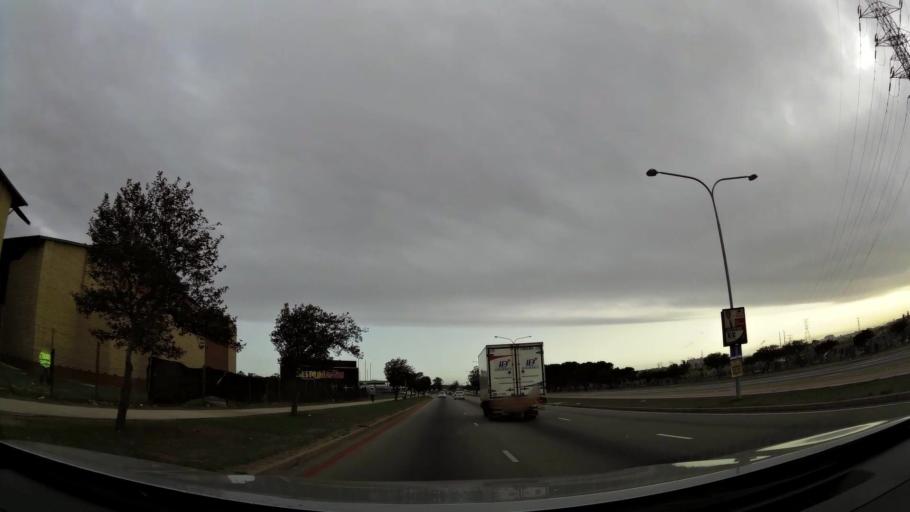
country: ZA
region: Eastern Cape
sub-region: Nelson Mandela Bay Metropolitan Municipality
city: Port Elizabeth
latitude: -33.9218
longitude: 25.5658
